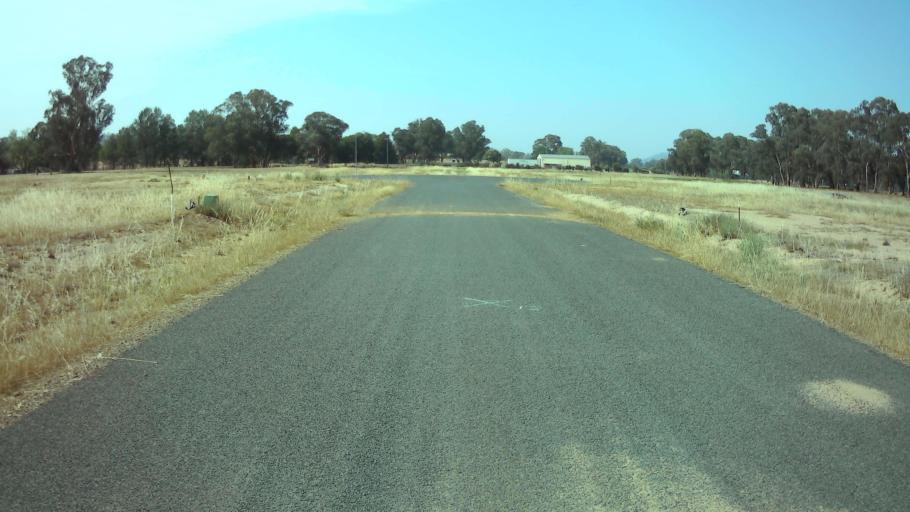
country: AU
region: New South Wales
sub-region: Weddin
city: Grenfell
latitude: -33.9019
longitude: 148.1486
